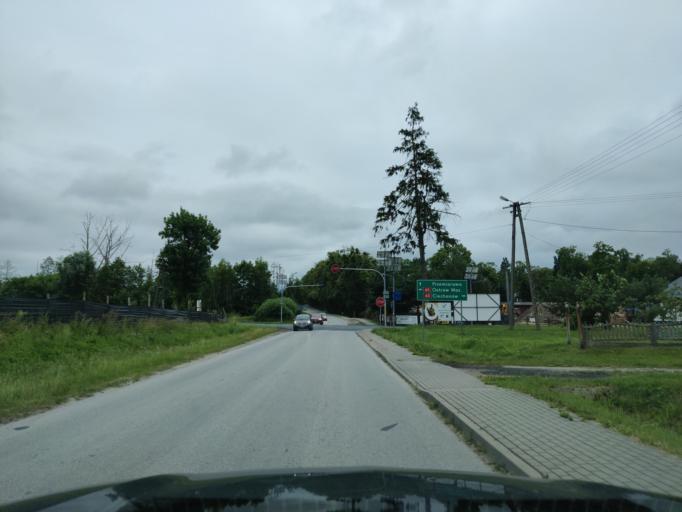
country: PL
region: Masovian Voivodeship
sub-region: Powiat makowski
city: Karniewo
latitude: 52.8395
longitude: 20.9868
